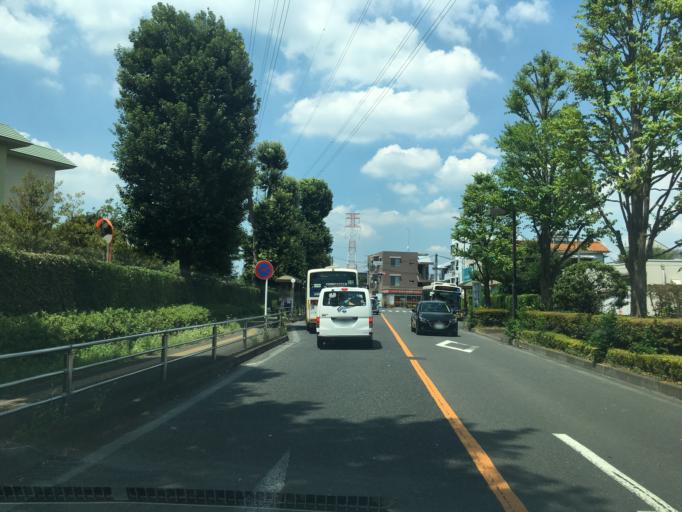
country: JP
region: Tokyo
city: Kokubunji
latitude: 35.6934
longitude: 139.4627
